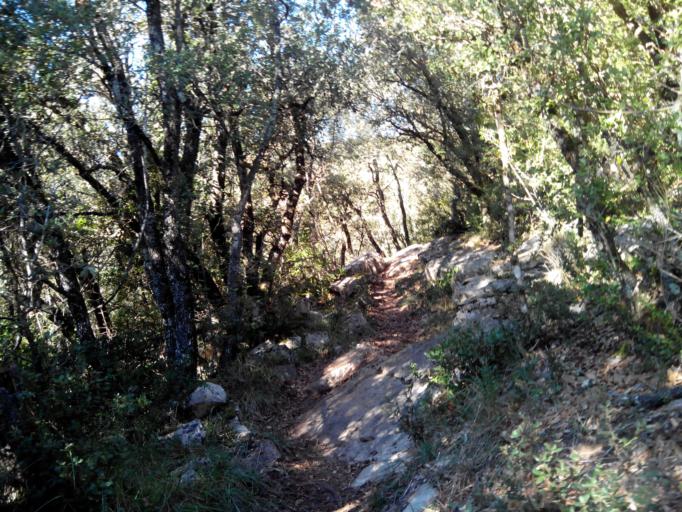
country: ES
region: Catalonia
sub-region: Provincia de Barcelona
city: Vilada
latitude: 42.1066
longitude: 1.9325
